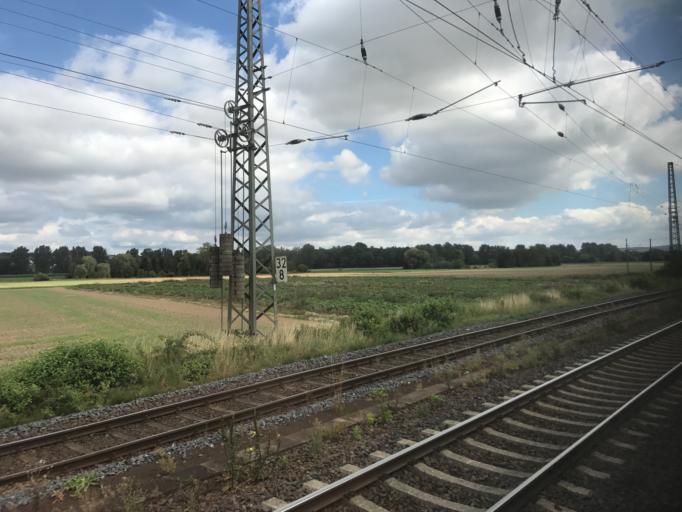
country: DE
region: Hesse
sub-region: Regierungsbezirk Kassel
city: Wabern
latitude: 51.1088
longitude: 9.3702
